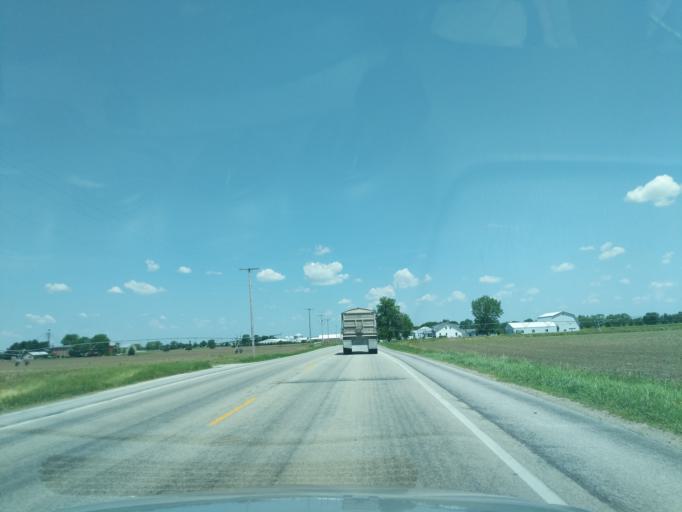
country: US
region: Indiana
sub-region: LaGrange County
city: Topeka
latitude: 41.5161
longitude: -85.5779
